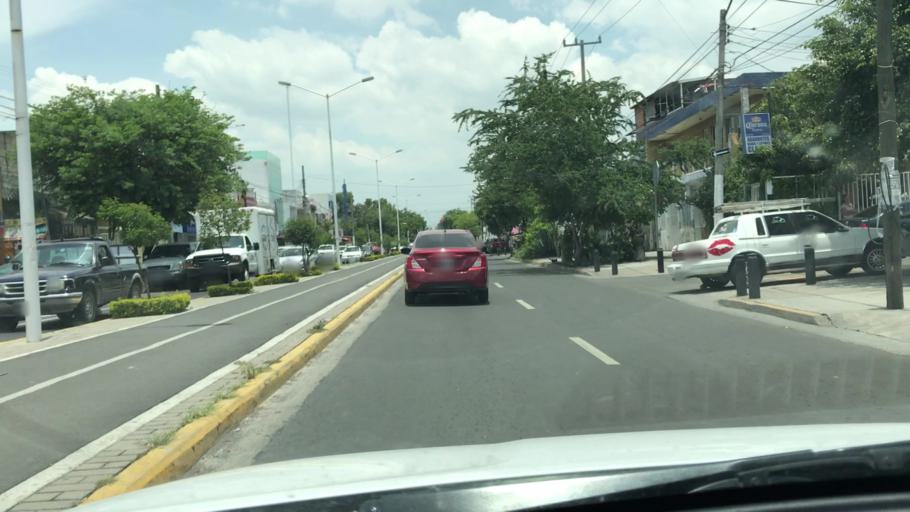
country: MX
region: Jalisco
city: Zapopan2
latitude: 20.7315
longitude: -103.4069
